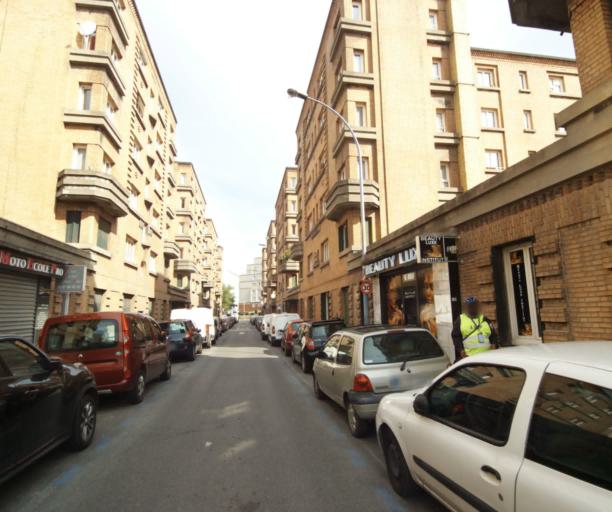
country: FR
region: Ile-de-France
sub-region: Departement du Val-d'Oise
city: Bezons
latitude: 48.9122
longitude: 2.2266
